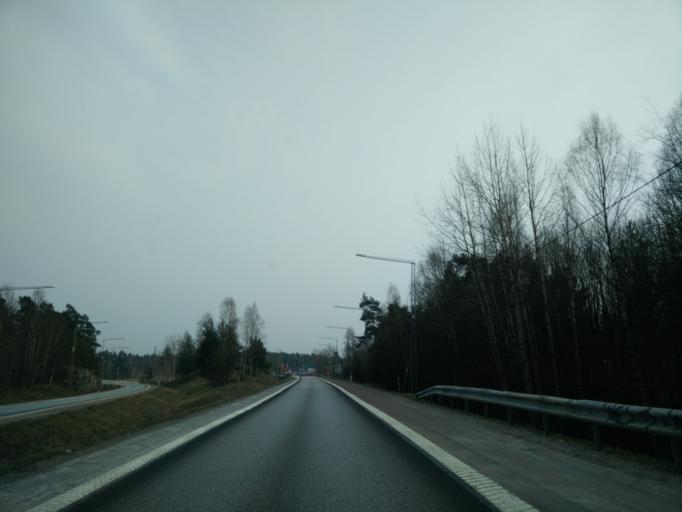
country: SE
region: Vaermland
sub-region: Hammaro Kommun
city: Skoghall
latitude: 59.3815
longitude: 13.4261
